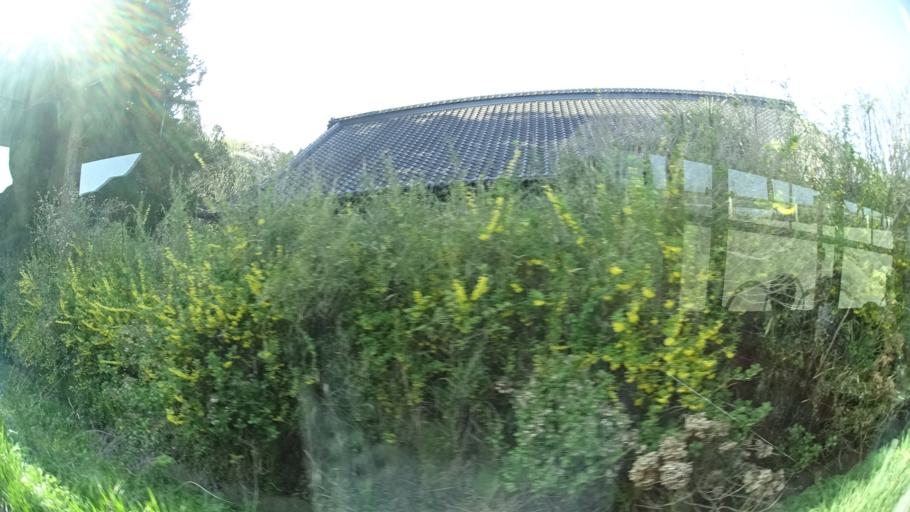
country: JP
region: Iwate
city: Ofunato
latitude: 39.0149
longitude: 141.6619
